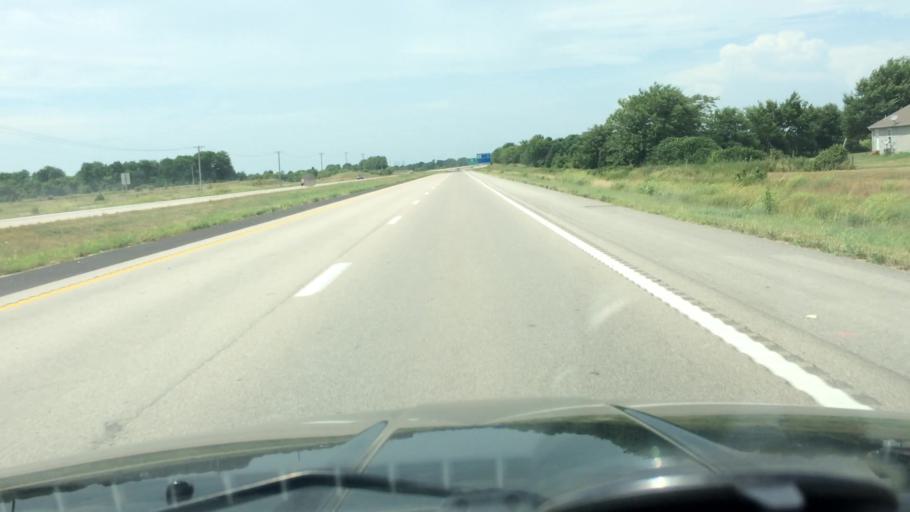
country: US
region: Missouri
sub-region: Polk County
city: Bolivar
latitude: 37.5872
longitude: -93.4214
